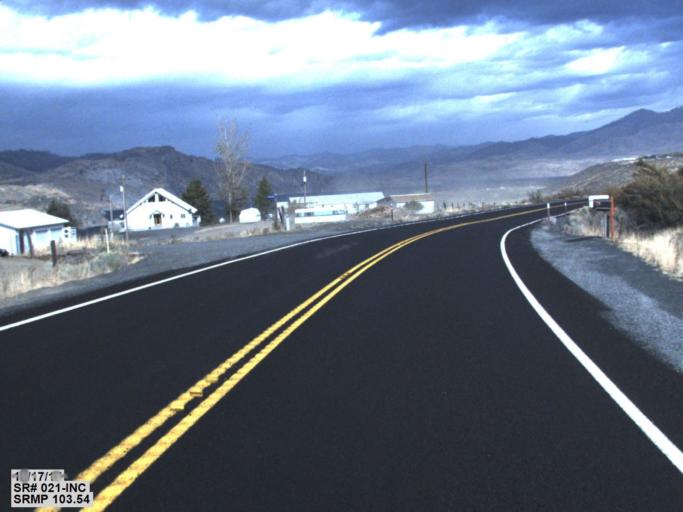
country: US
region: Washington
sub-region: Okanogan County
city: Coulee Dam
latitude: 47.8944
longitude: -118.7143
